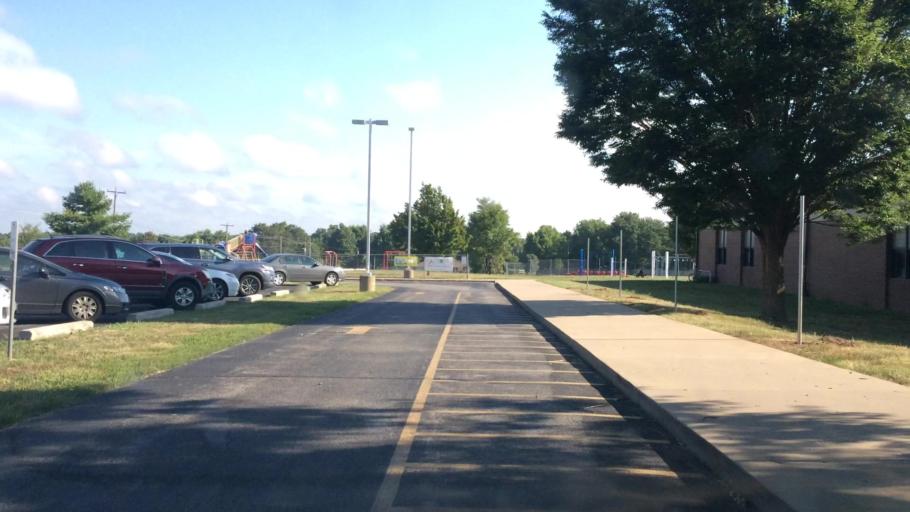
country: US
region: Missouri
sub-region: Greene County
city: Springfield
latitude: 37.2675
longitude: -93.2809
